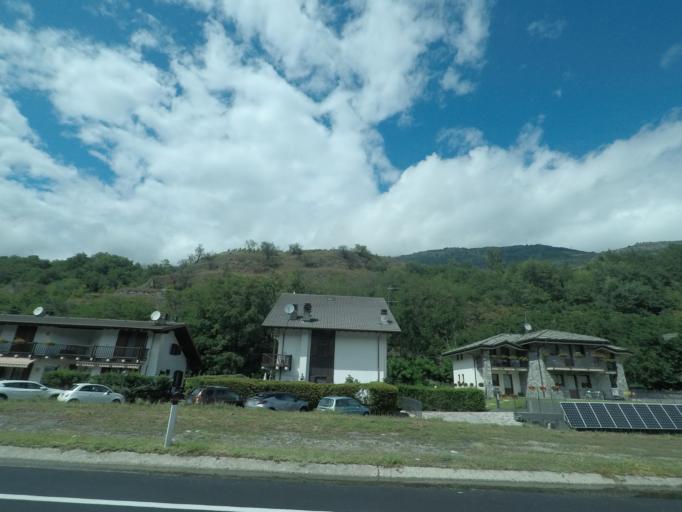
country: IT
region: Aosta Valley
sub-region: Valle d'Aosta
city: Villefranche
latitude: 45.7396
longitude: 7.4253
